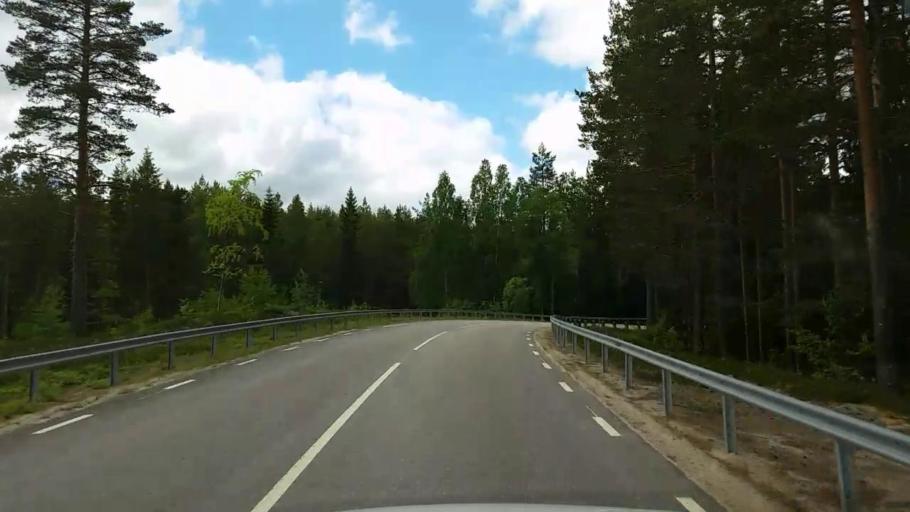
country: SE
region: Gaevleborg
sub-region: Bollnas Kommun
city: Vittsjo
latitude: 61.1391
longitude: 16.1700
